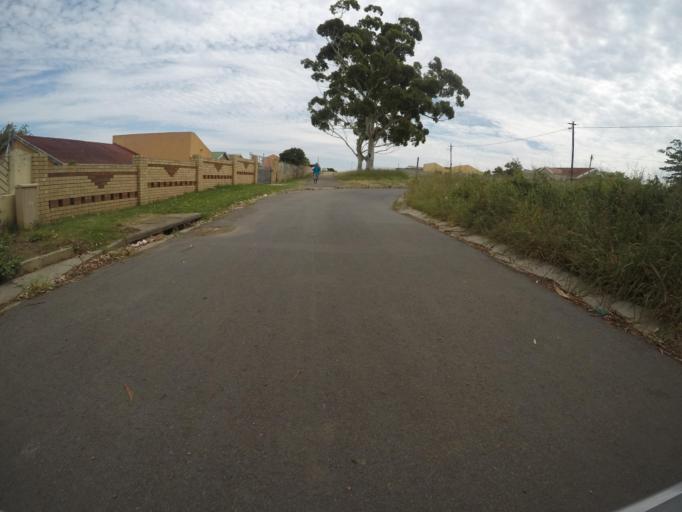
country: ZA
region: Eastern Cape
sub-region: Buffalo City Metropolitan Municipality
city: East London
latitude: -33.0003
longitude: 27.8741
